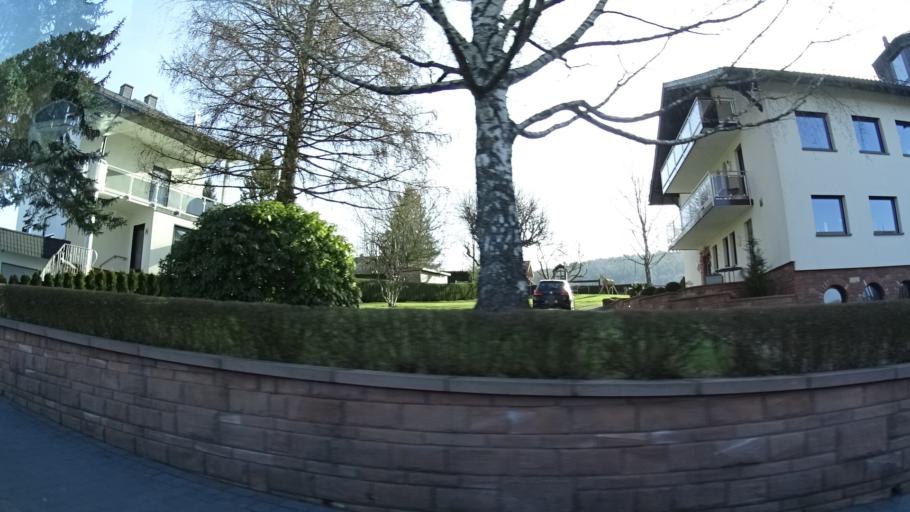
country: DE
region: Hesse
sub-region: Regierungsbezirk Darmstadt
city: Wald-Michelbach
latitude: 49.6115
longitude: 8.8560
